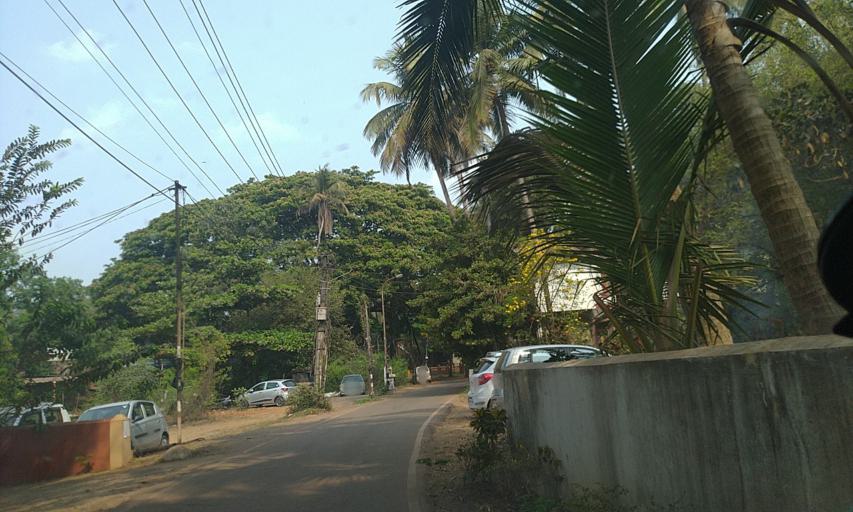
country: IN
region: Goa
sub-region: North Goa
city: Taleigao
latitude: 15.4764
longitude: 73.8432
